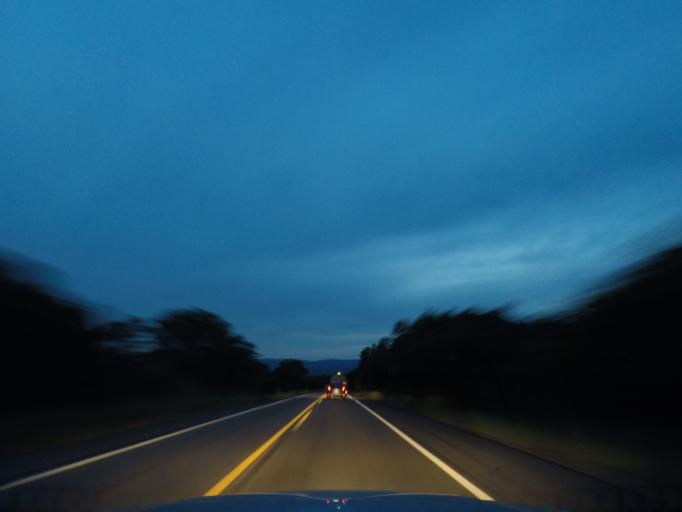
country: BR
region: Bahia
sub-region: Andarai
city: Vera Cruz
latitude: -12.4945
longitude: -41.3054
